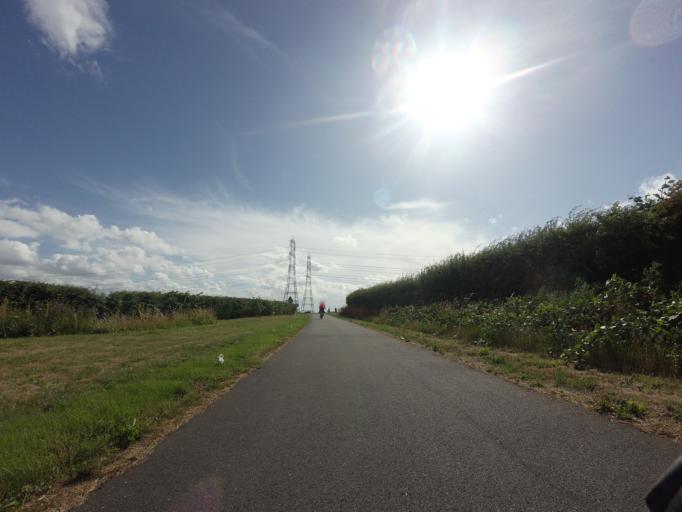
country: GB
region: England
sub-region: Kent
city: Hoo
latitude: 51.4295
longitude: 0.5836
